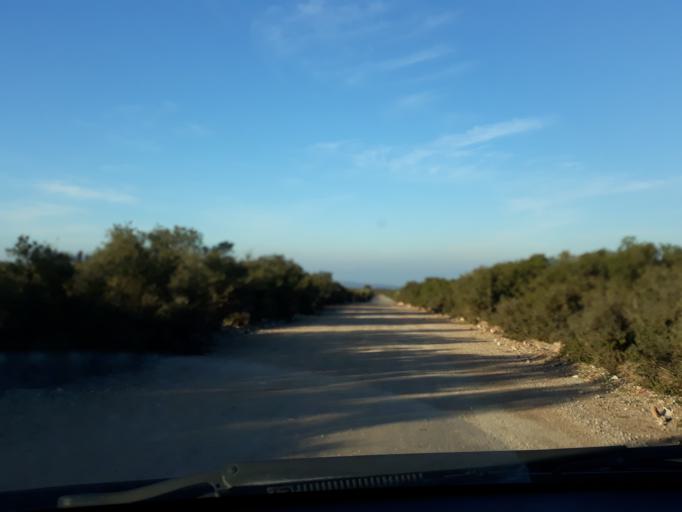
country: GR
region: Central Greece
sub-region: Nomos Voiotias
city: Asopia
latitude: 38.2399
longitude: 23.5334
